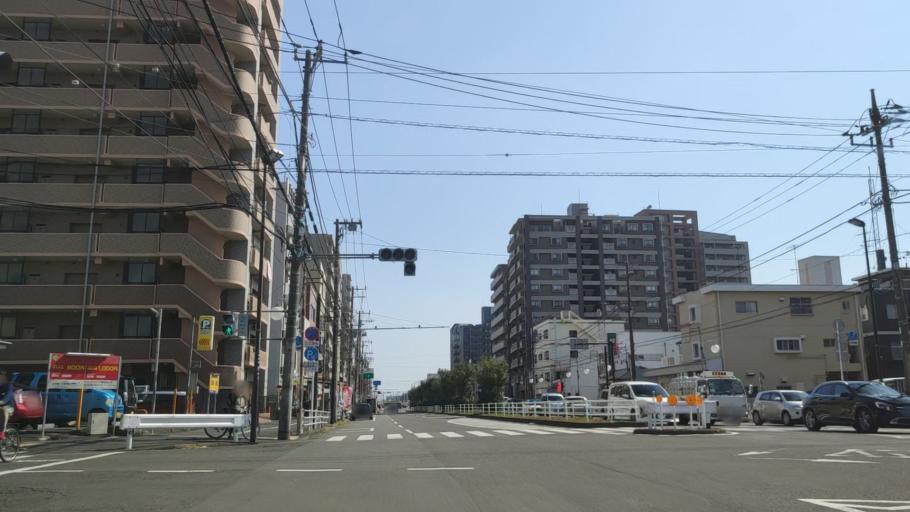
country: JP
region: Kanagawa
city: Hiratsuka
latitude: 35.3311
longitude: 139.3449
